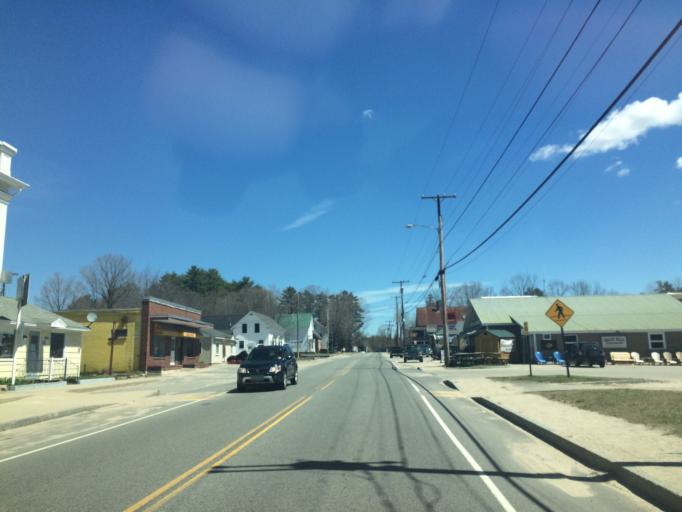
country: US
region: Maine
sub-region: Oxford County
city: Porter
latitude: 43.8065
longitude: -70.8875
